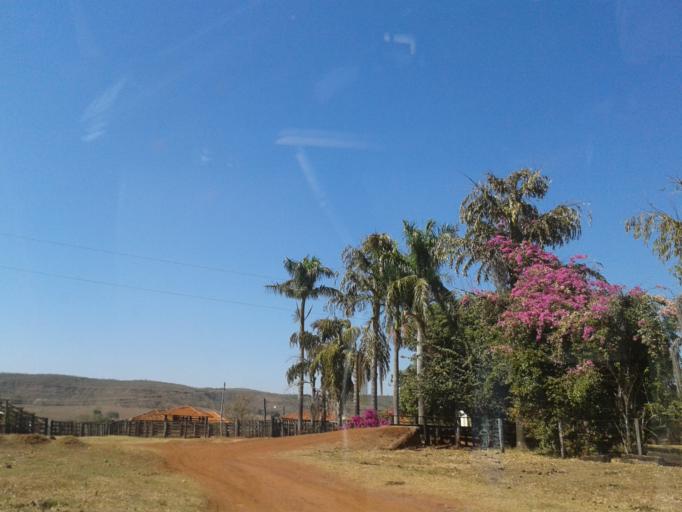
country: BR
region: Minas Gerais
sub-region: Santa Vitoria
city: Santa Vitoria
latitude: -19.1053
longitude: -49.9810
